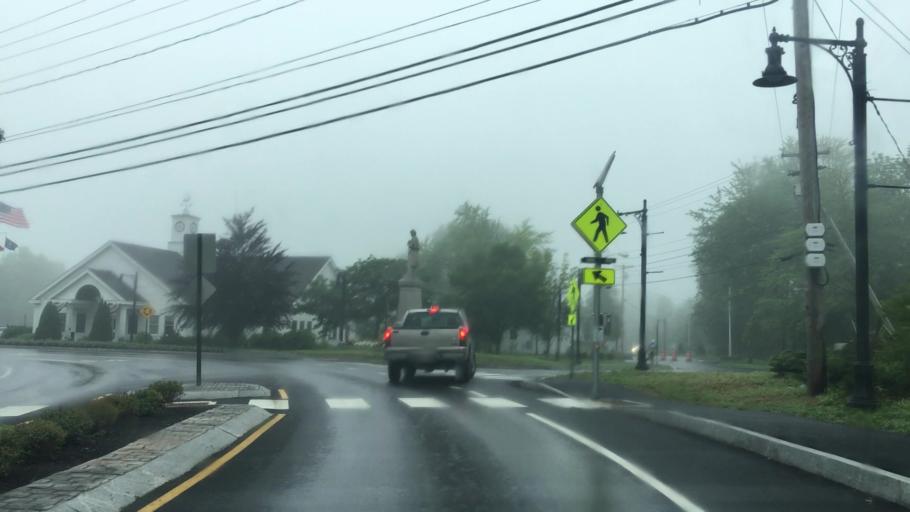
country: US
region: Maine
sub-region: Lincoln County
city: Boothbay
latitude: 43.8764
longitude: -69.6339
